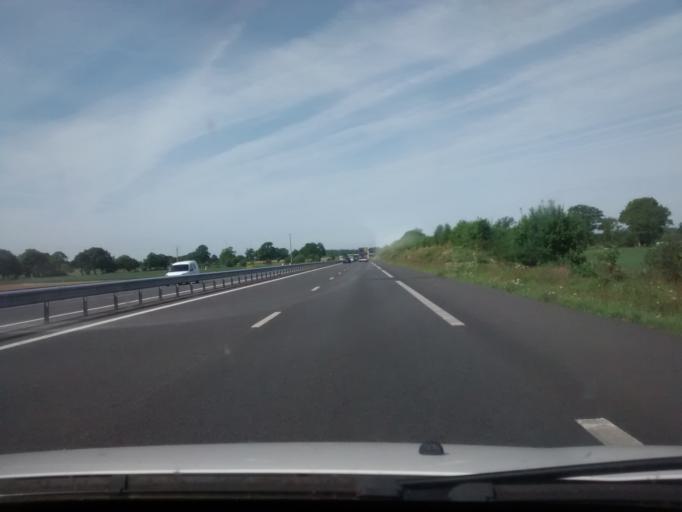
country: FR
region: Brittany
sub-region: Departement d'Ille-et-Vilaine
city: Romagne
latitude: 48.3535
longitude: -1.2646
